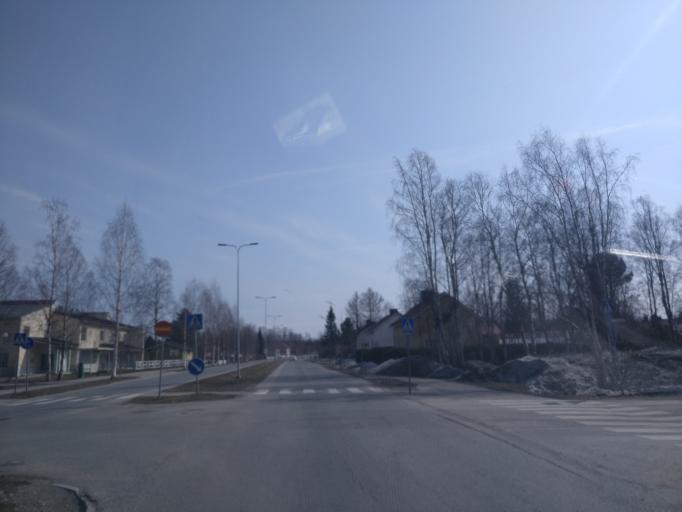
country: FI
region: Lapland
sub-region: Kemi-Tornio
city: Kemi
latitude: 65.7291
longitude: 24.6054
